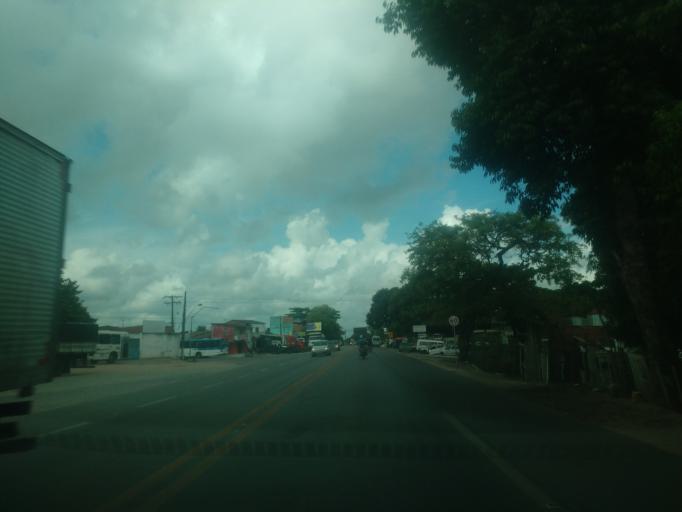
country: BR
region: Alagoas
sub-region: Satuba
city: Satuba
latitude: -9.5652
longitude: -35.7899
